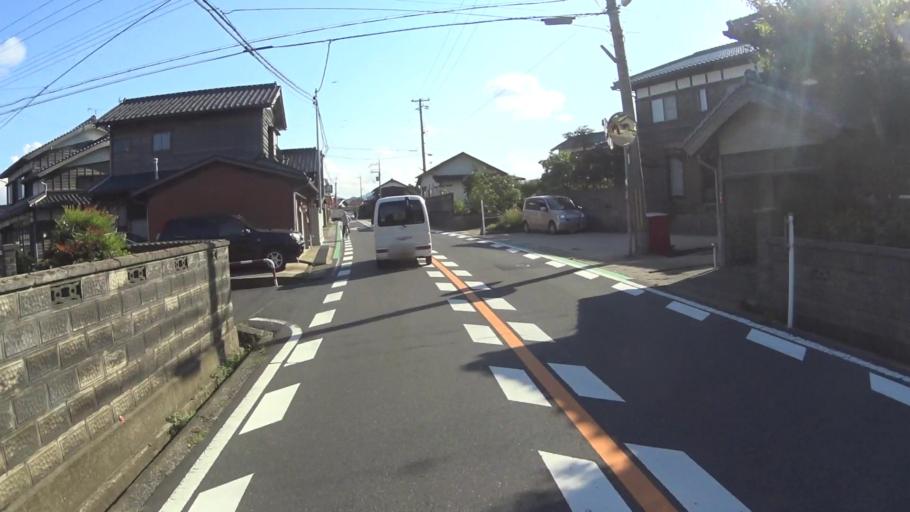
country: JP
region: Kyoto
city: Miyazu
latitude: 35.6912
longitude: 135.0351
